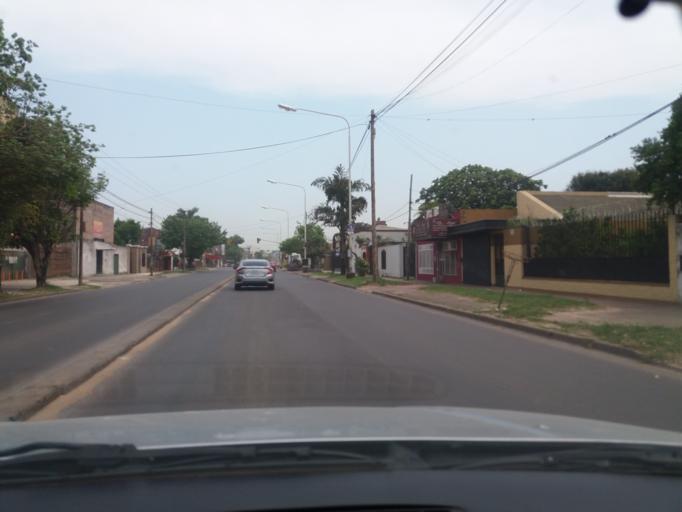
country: AR
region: Corrientes
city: Corrientes
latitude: -27.4929
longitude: -58.8187
